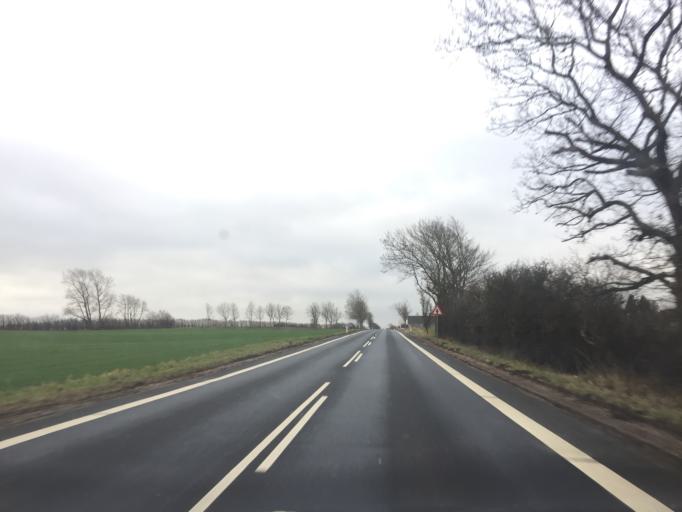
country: DK
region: South Denmark
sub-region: Svendborg Kommune
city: Thuro By
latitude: 55.1342
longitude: 10.6710
